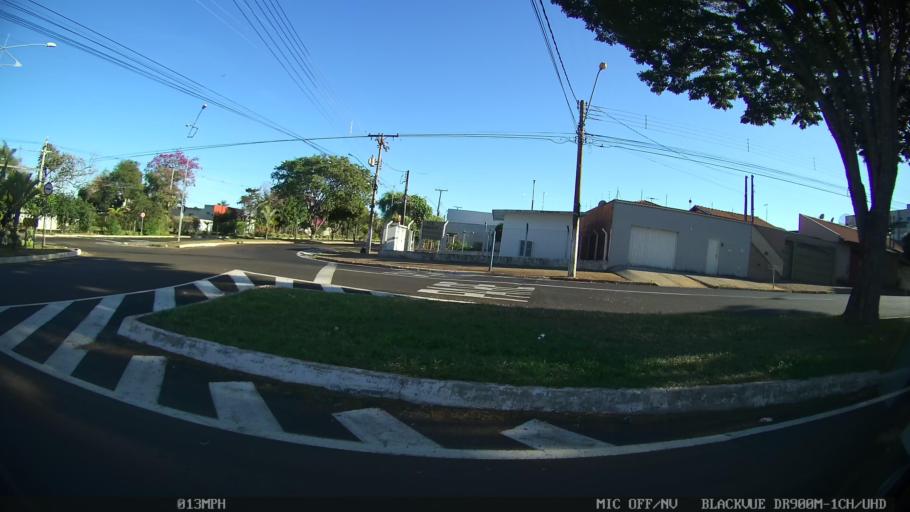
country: BR
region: Sao Paulo
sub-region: Franca
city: Franca
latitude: -20.5826
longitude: -47.3830
